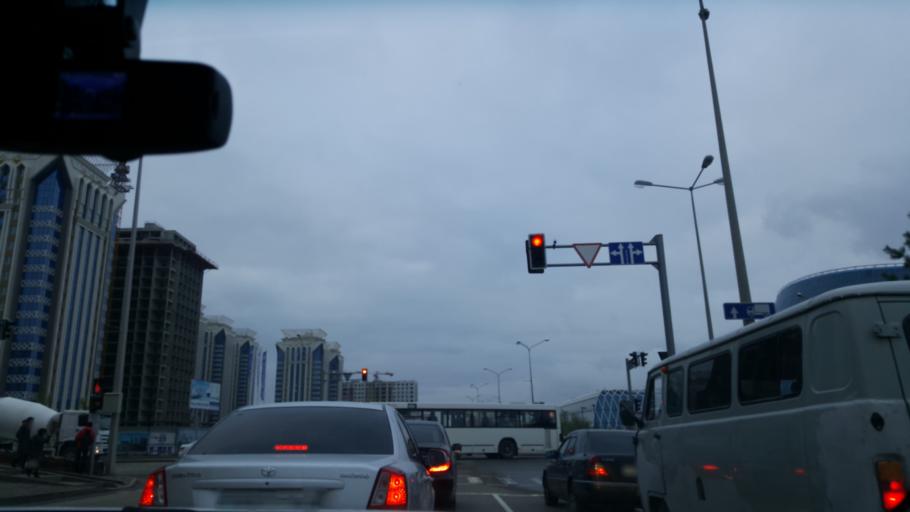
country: KZ
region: Astana Qalasy
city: Astana
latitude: 51.1241
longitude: 71.4755
